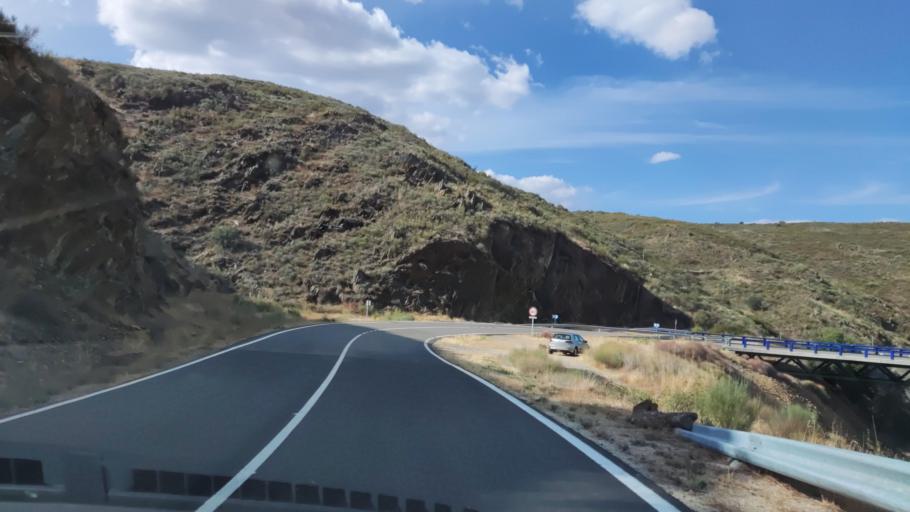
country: ES
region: Castille and Leon
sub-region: Provincia de Salamanca
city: Pastores
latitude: 40.4964
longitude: -6.4972
